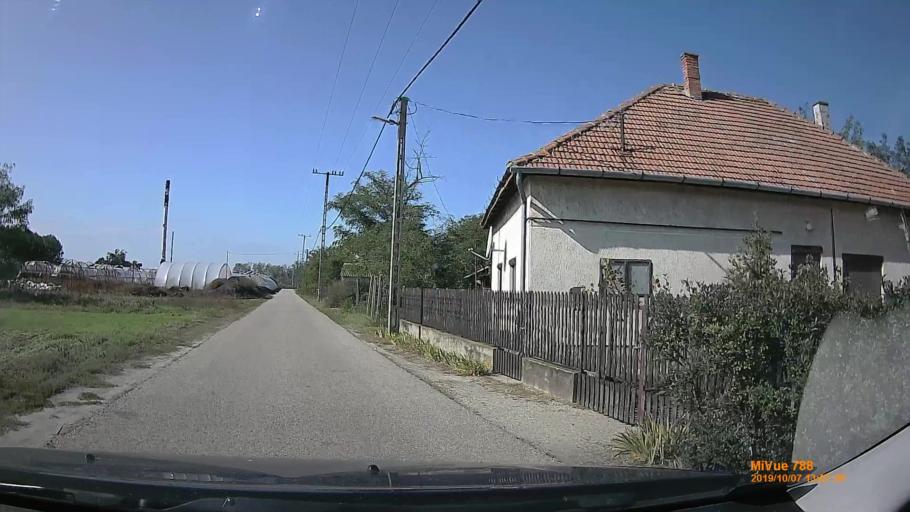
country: HU
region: Jasz-Nagykun-Szolnok
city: Cserkeszolo
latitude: 46.8730
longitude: 20.1843
